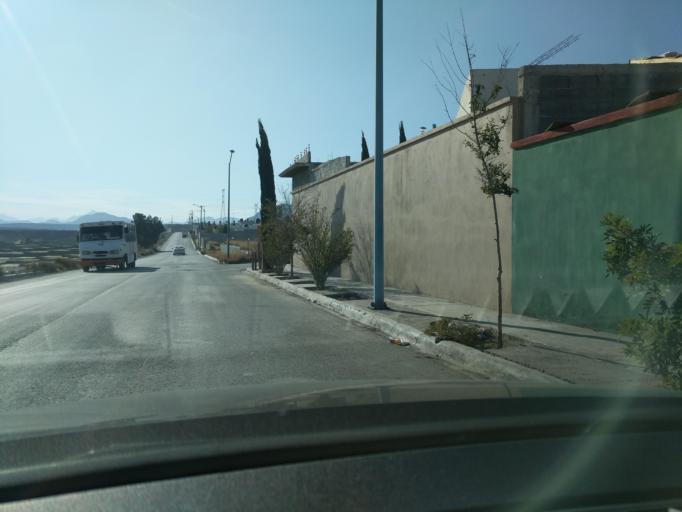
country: MX
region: Coahuila
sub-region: Ramos Arizpe
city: Ramos Arizpe
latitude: 25.5426
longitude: -100.9727
